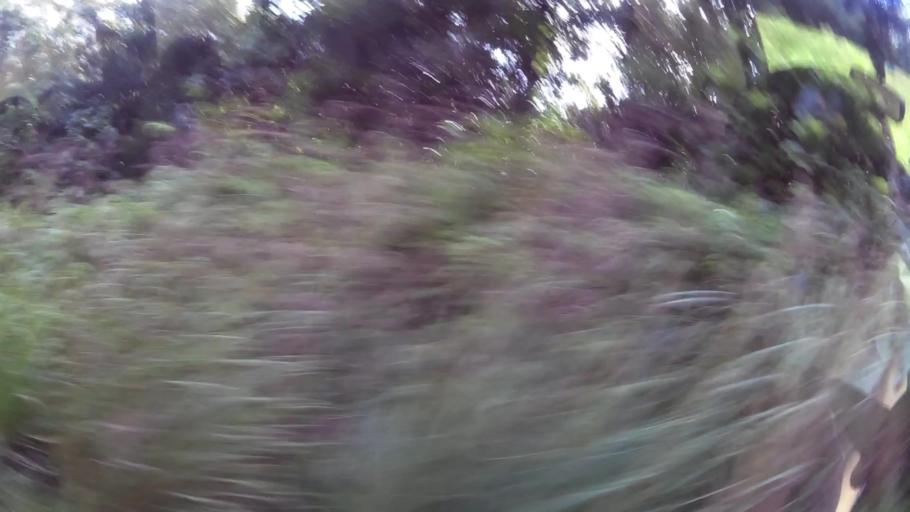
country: DM
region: Saint Paul
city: Pont Casse
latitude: 15.3860
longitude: -61.3374
